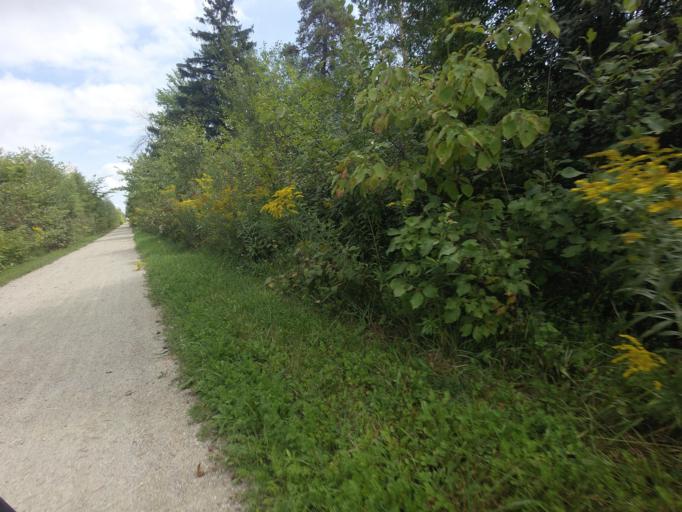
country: CA
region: Ontario
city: North Perth
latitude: 43.5757
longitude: -80.8163
